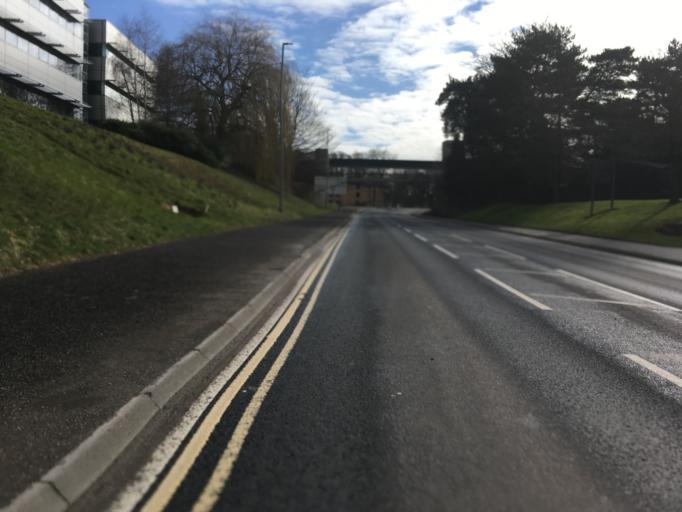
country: GB
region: England
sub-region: City of York
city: Heslington
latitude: 53.9481
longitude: -1.0496
